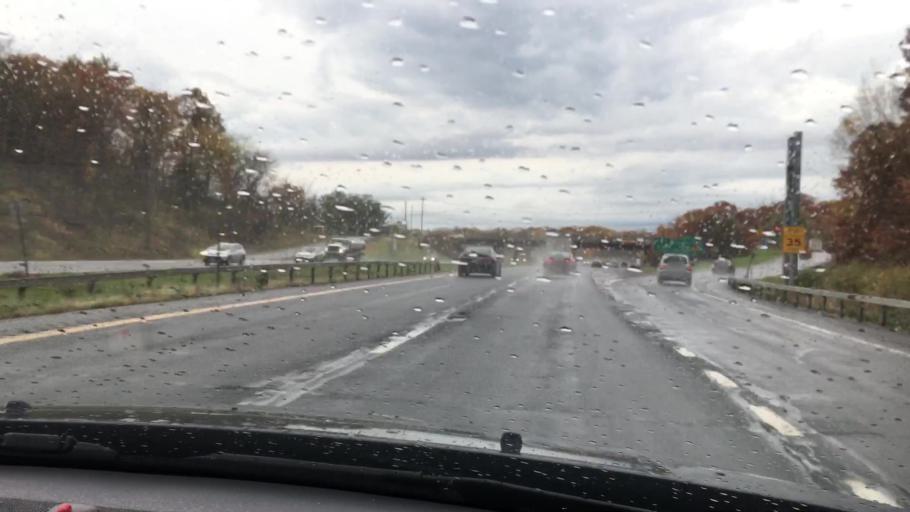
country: US
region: New York
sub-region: Orange County
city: Gardnertown
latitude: 41.5143
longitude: -74.0452
